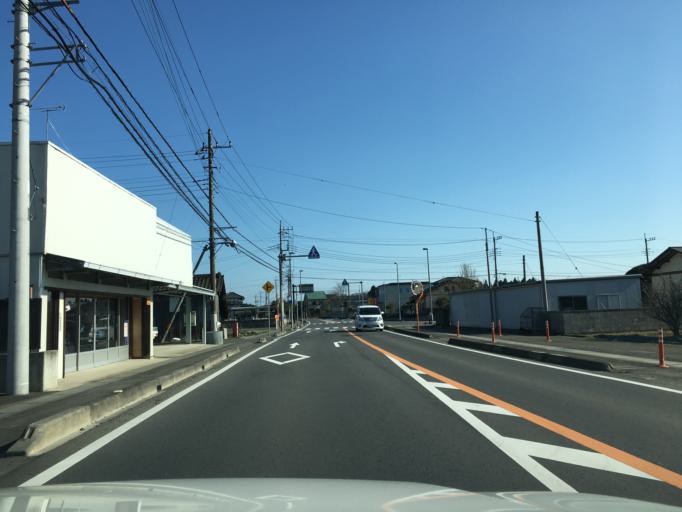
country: JP
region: Ibaraki
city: Omiya
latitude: 36.4630
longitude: 140.4002
